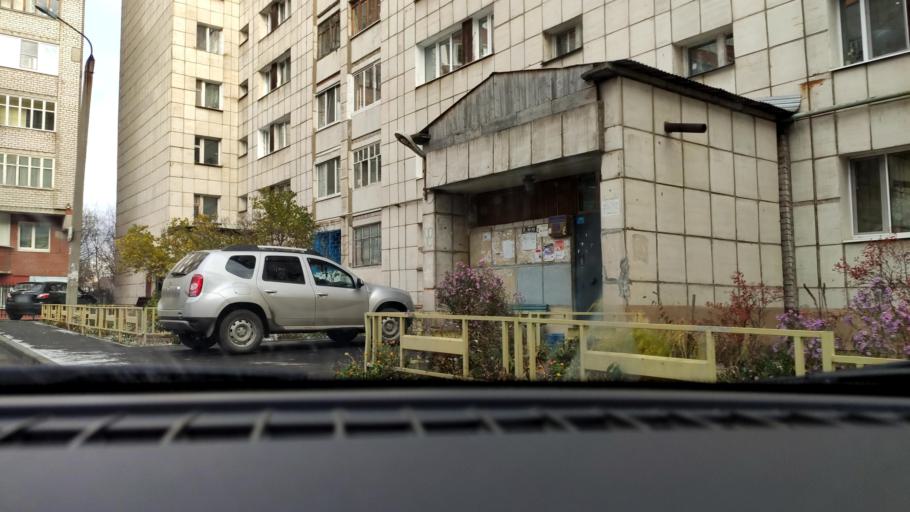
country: RU
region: Perm
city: Perm
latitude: 57.9799
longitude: 56.2786
